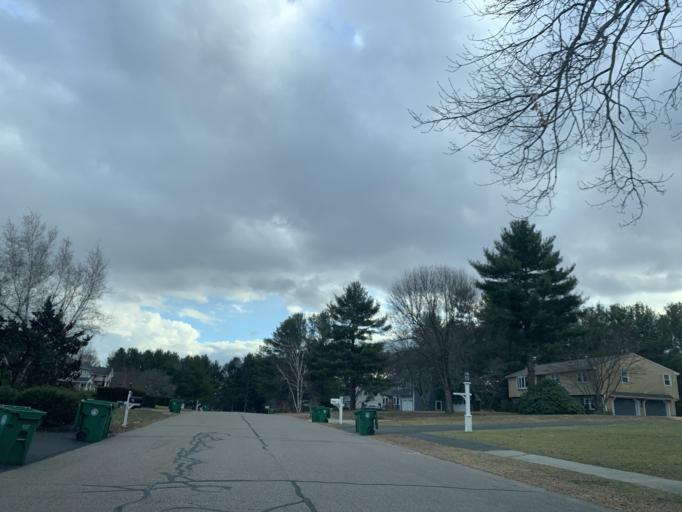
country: US
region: Massachusetts
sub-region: Norfolk County
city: Dedham
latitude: 42.2122
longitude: -71.1583
